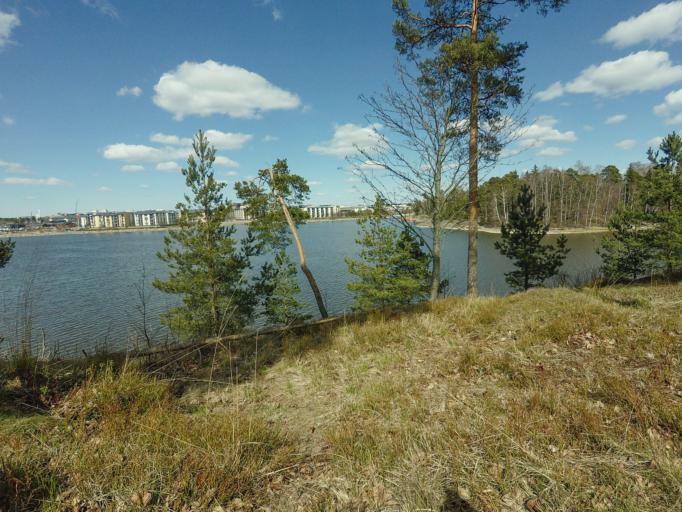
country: FI
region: Uusimaa
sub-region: Helsinki
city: Helsinki
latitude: 60.1813
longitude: 25.0319
